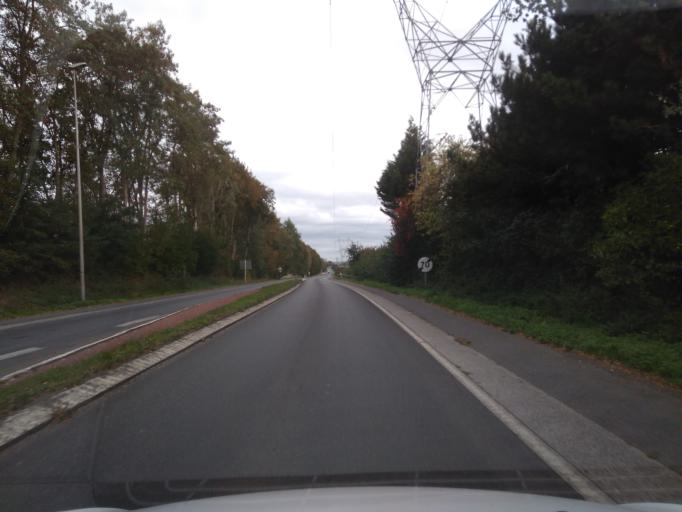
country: FR
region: Nord-Pas-de-Calais
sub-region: Departement du Nord
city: Saint-Saulve
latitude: 50.3617
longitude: 3.5641
